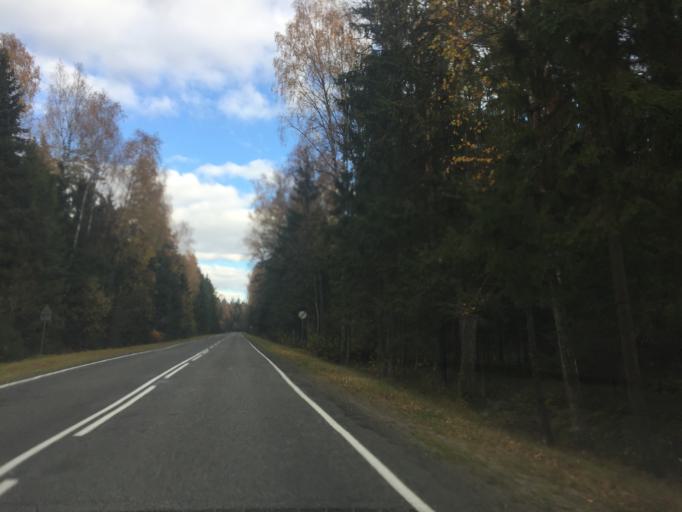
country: BY
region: Minsk
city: Svir
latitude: 54.9253
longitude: 26.5384
